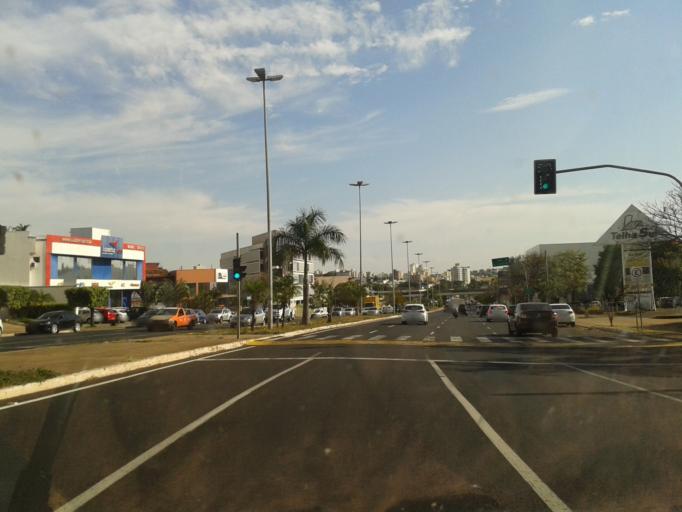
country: BR
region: Minas Gerais
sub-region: Uberlandia
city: Uberlandia
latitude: -18.9278
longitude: -48.2753
